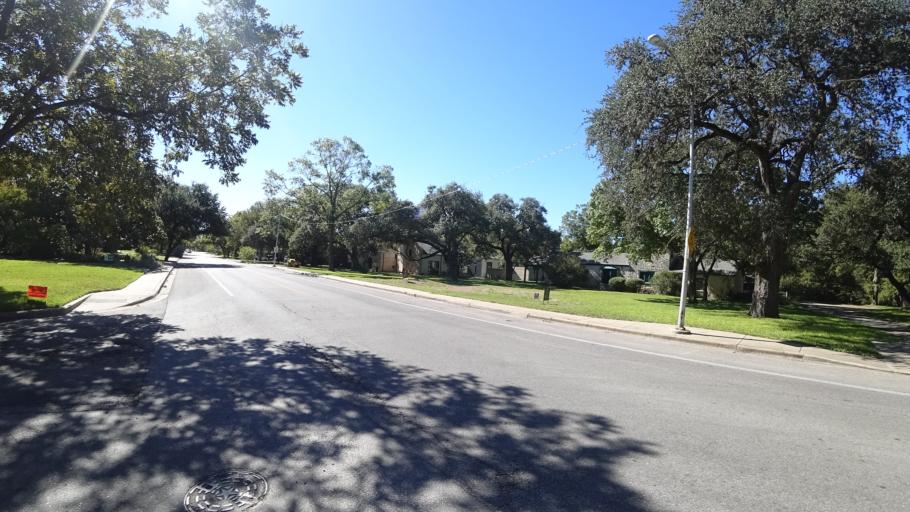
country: US
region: Texas
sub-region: Travis County
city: Austin
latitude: 30.3280
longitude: -97.7455
